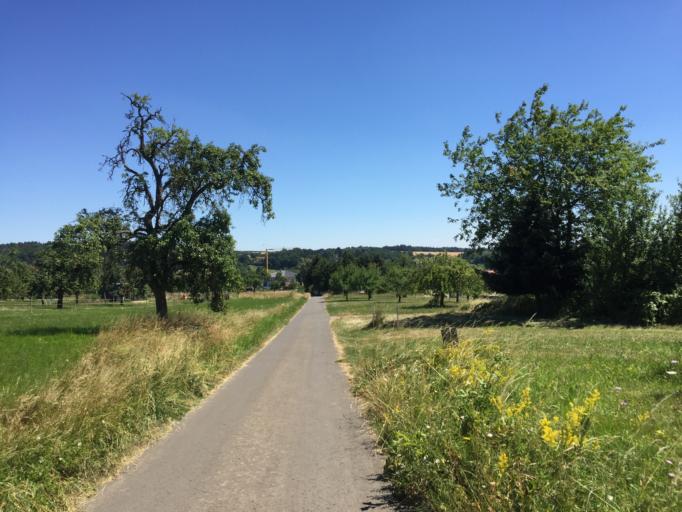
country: DE
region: Hesse
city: Beuern
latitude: 50.6323
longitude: 8.8157
